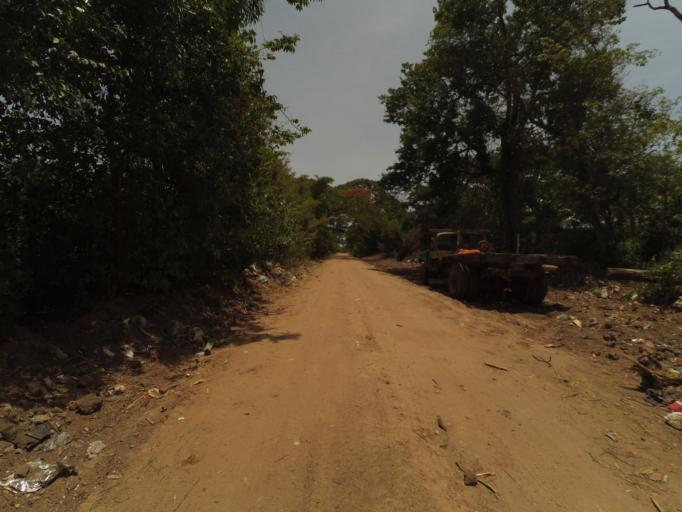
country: BO
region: Santa Cruz
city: Santa Cruz de la Sierra
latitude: -17.8269
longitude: -63.2527
